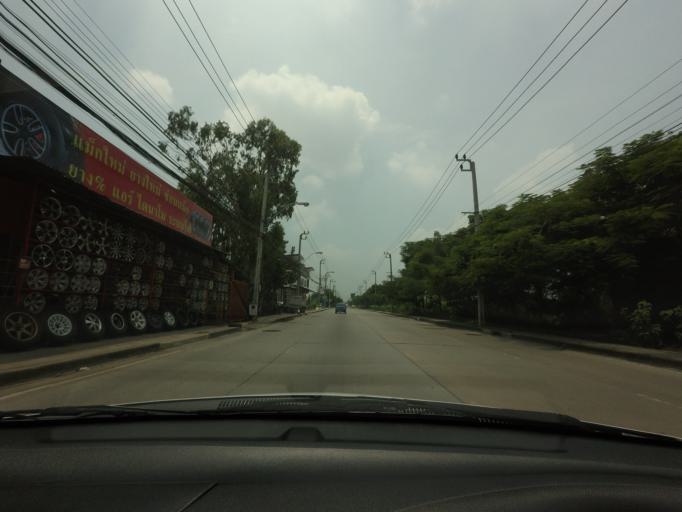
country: TH
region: Bangkok
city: Bang Na
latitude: 13.6649
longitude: 100.6825
